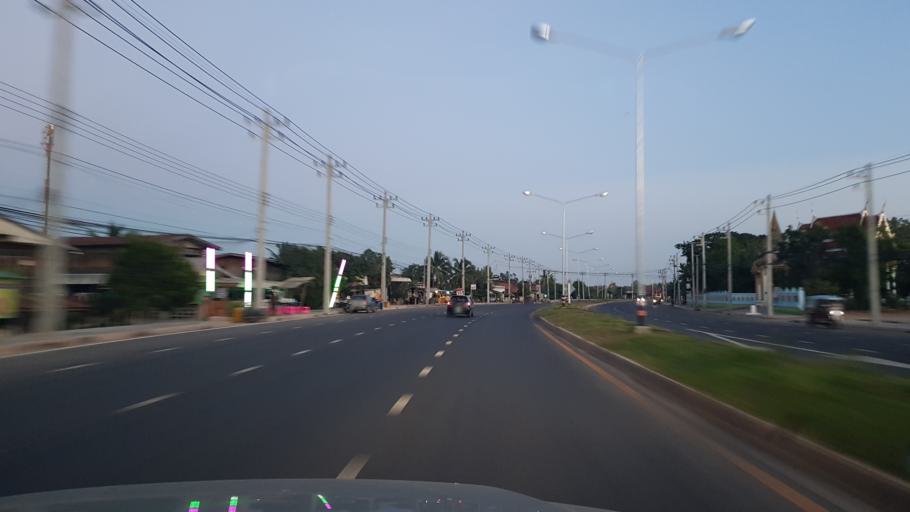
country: TH
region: Chaiyaphum
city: Phu Khiao
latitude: 16.3617
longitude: 102.1464
